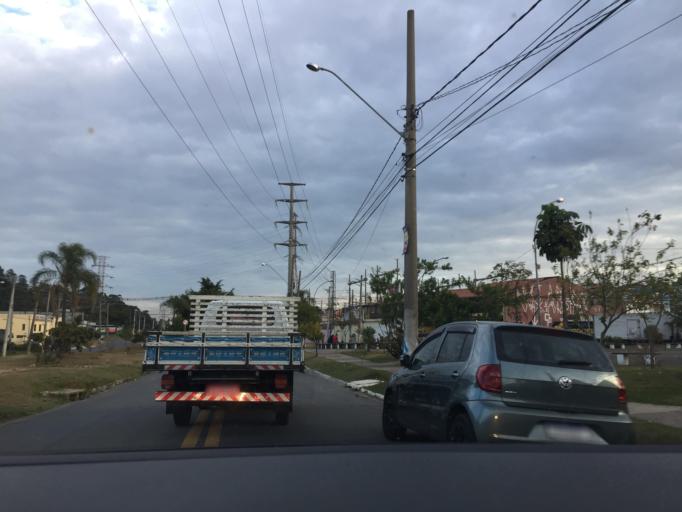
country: BR
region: Sao Paulo
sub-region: Varzea Paulista
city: Varzea Paulista
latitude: -23.2112
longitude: -46.8396
